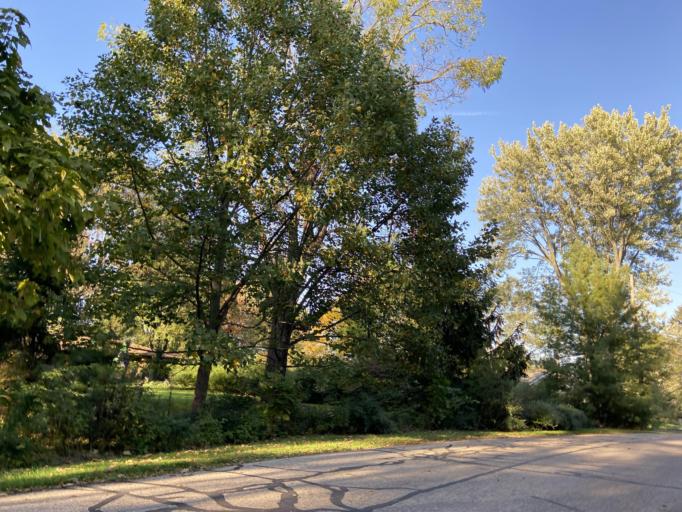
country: US
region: Michigan
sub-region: Oakland County
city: Franklin
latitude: 42.5108
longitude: -83.3327
